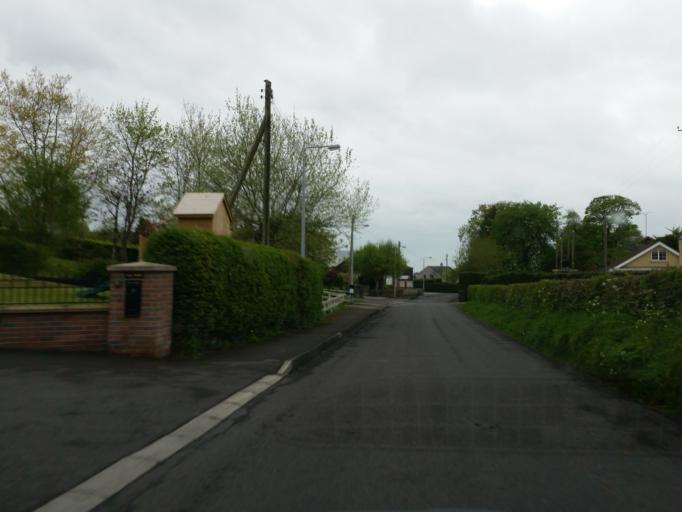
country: GB
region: Northern Ireland
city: Lisnaskea
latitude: 54.2427
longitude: -7.4406
